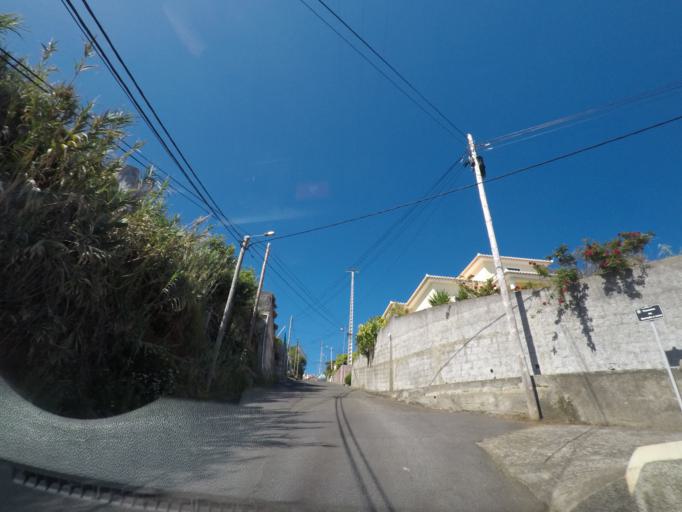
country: PT
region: Madeira
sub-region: Calheta
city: Arco da Calheta
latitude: 32.7018
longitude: -17.1168
